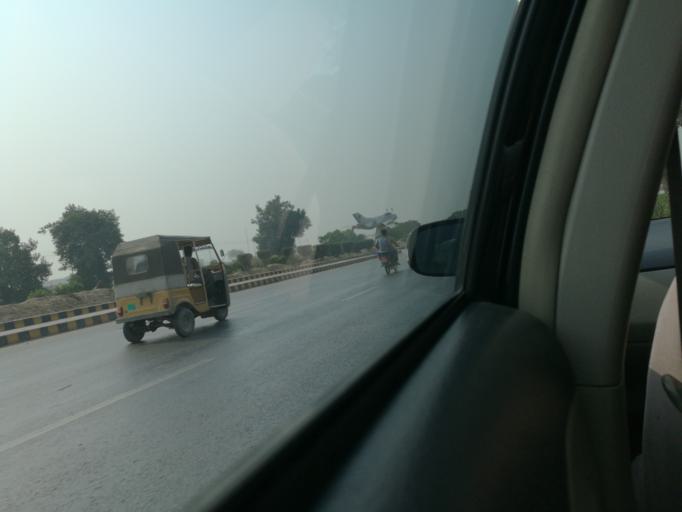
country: PK
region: Sindh
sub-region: Karachi District
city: Karachi
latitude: 24.8782
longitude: 67.1051
